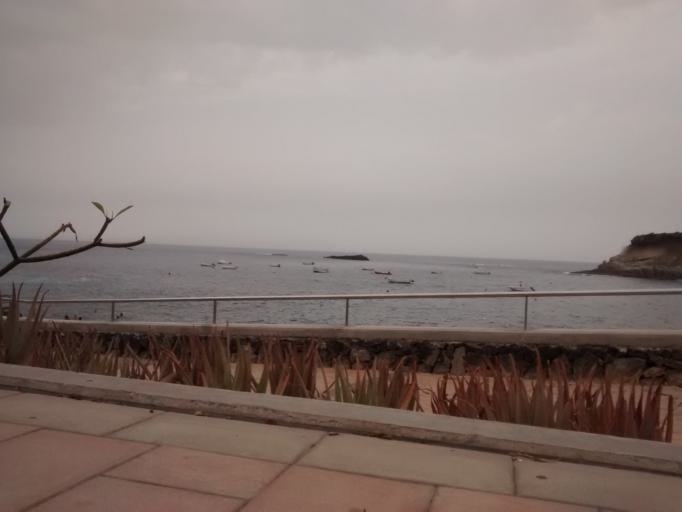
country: ES
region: Canary Islands
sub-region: Provincia de Santa Cruz de Tenerife
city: Adeje
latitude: 28.0994
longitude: -16.7559
